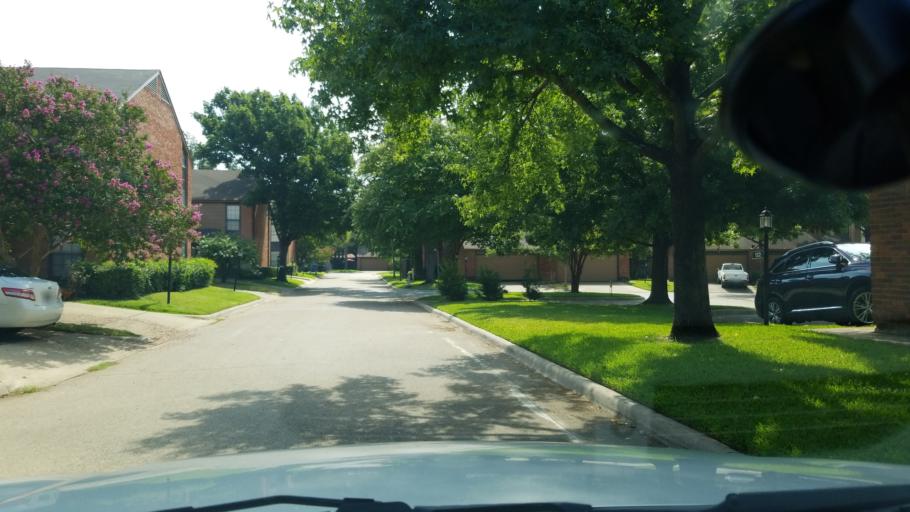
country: US
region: Texas
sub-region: Dallas County
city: Irving
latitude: 32.8347
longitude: -96.9264
